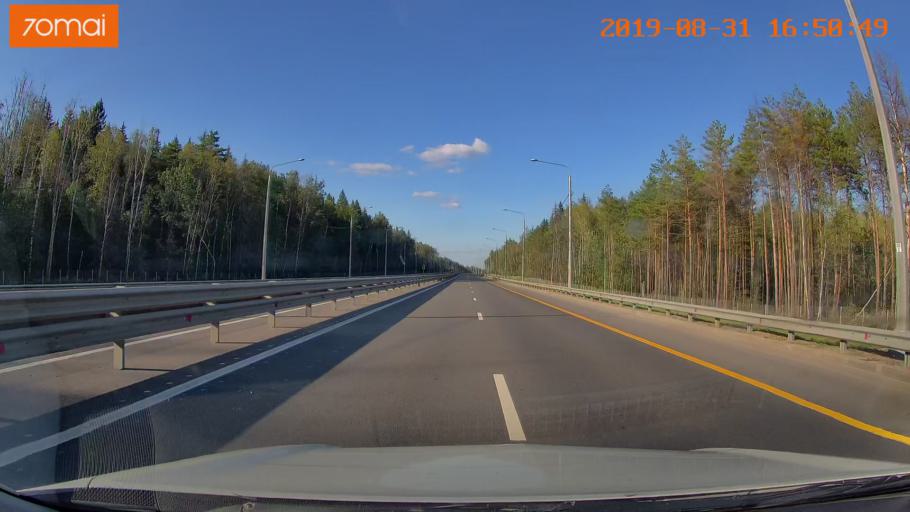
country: RU
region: Kaluga
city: Pyatovskiy
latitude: 54.7154
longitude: 36.1656
